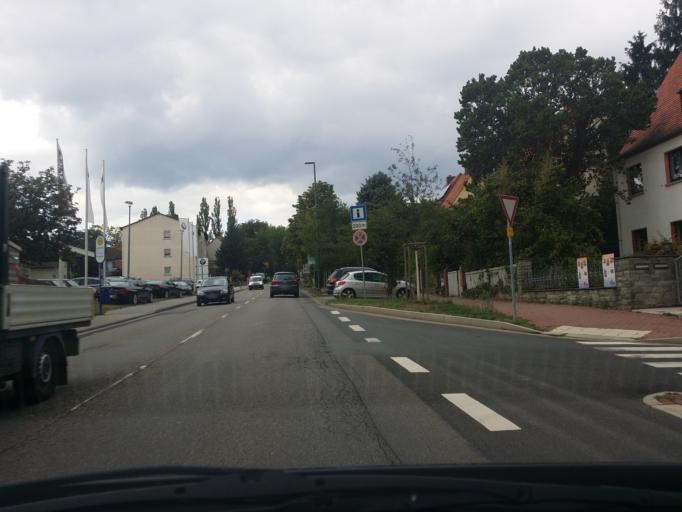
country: DE
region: Hesse
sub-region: Regierungsbezirk Darmstadt
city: Kronberg
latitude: 50.1747
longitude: 8.5229
